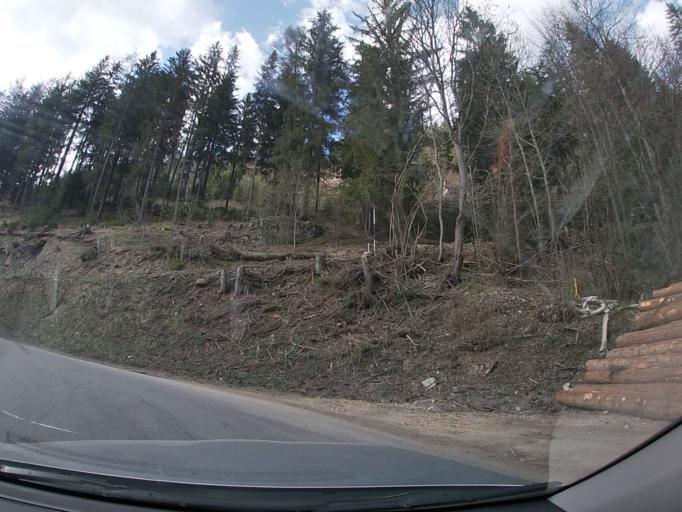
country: AT
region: Styria
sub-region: Politischer Bezirk Murau
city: Murau
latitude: 47.1131
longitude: 14.2002
